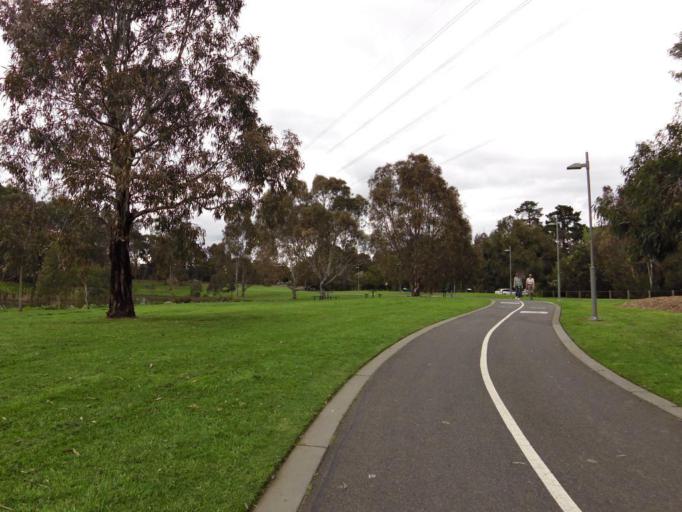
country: AU
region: Victoria
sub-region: Stonnington
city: Glen Iris
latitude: -37.8664
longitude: 145.0640
